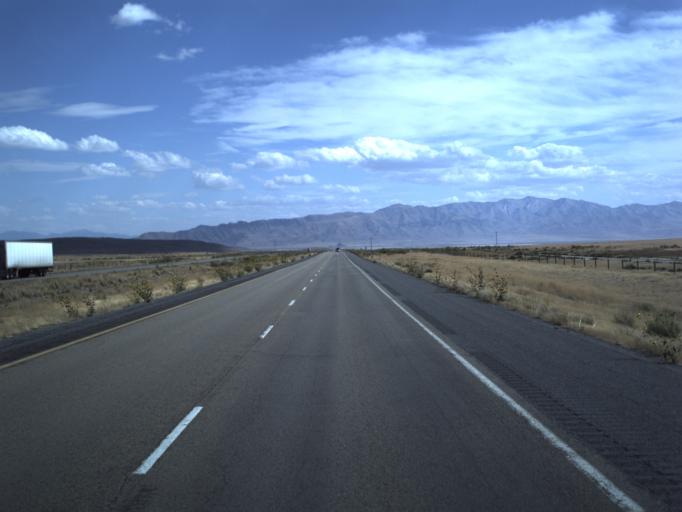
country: US
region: Utah
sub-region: Tooele County
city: Grantsville
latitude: 40.8028
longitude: -112.8548
